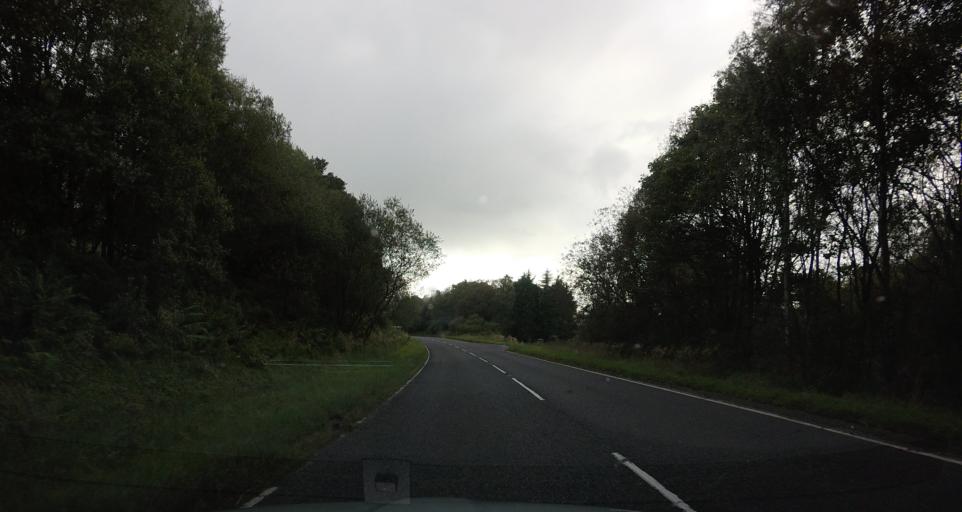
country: GB
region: Scotland
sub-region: Fife
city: Saline
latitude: 56.1609
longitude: -3.6051
